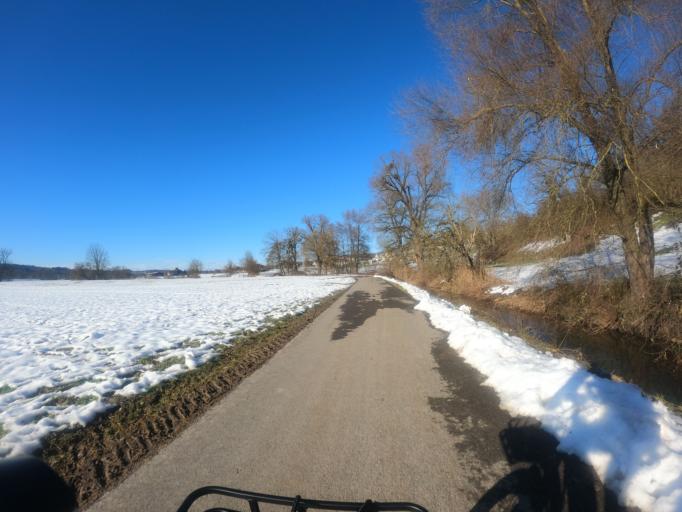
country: CH
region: Aargau
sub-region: Bezirk Bremgarten
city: Unterlunkhofen
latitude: 47.3153
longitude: 8.3842
